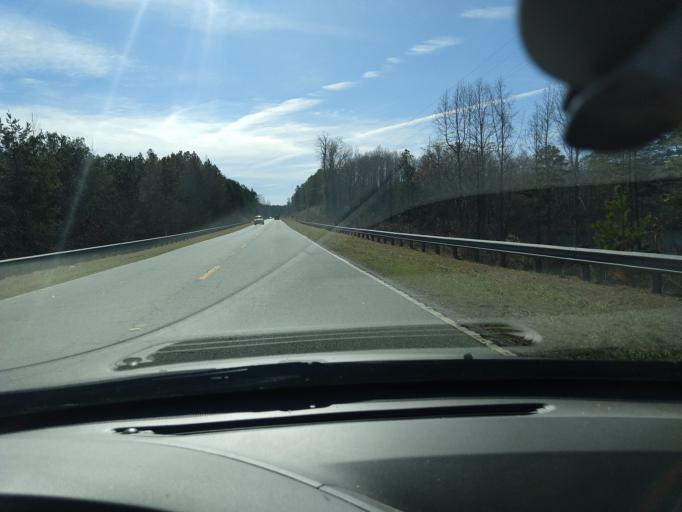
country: US
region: South Carolina
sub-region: Oconee County
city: Westminster
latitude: 34.6327
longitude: -83.1356
